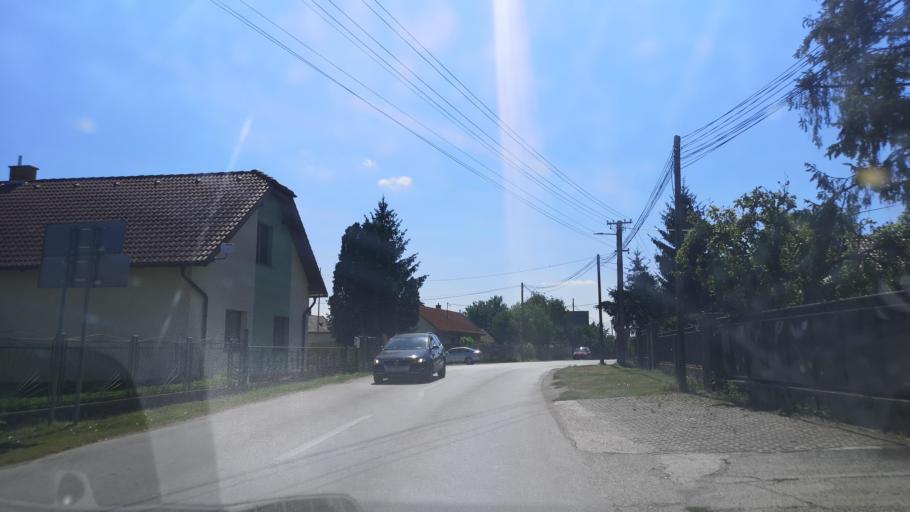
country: SK
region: Bratislavsky
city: Senec
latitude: 48.1011
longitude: 17.4762
